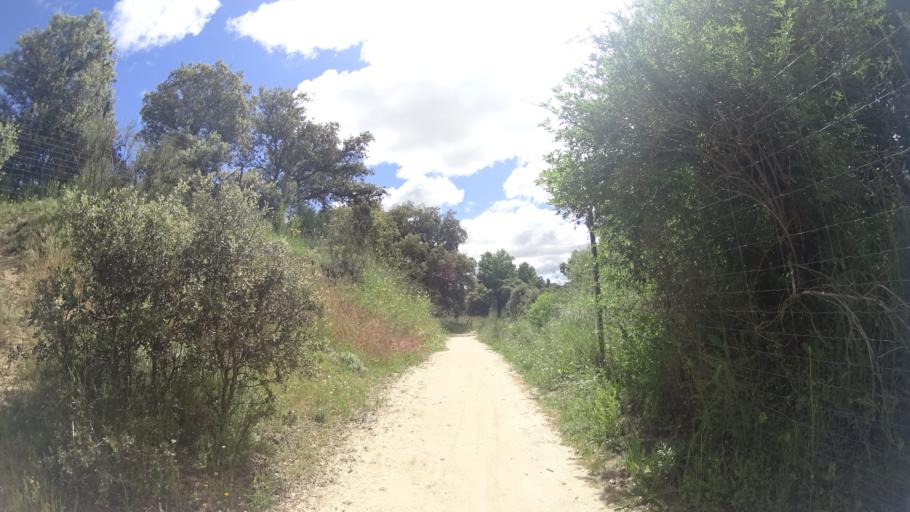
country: ES
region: Madrid
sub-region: Provincia de Madrid
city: Brunete
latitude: 40.3917
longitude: -3.9449
